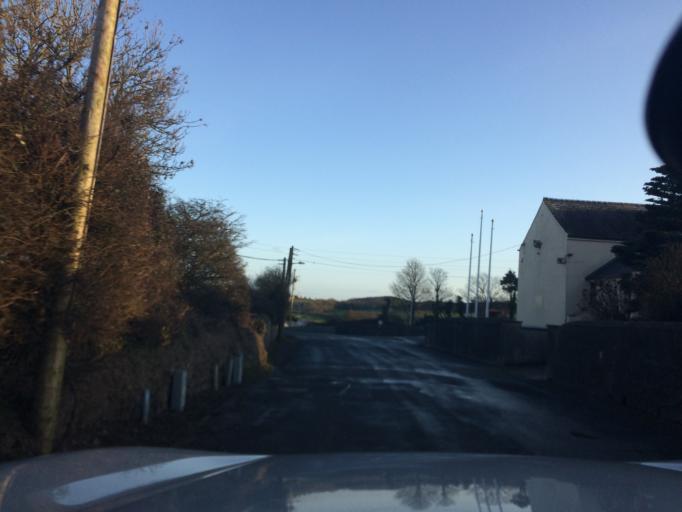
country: IE
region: Munster
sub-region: Waterford
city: Tra Mhor
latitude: 52.2254
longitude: -7.1817
